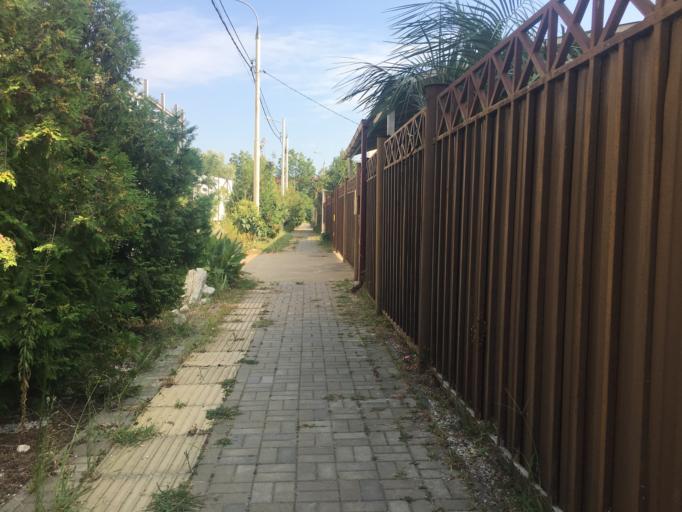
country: RU
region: Krasnodarskiy
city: Vysokoye
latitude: 43.3946
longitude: 40.0017
